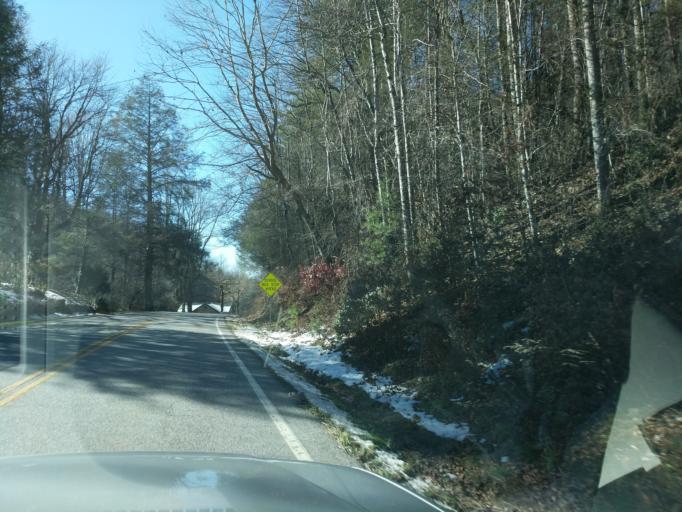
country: US
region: Georgia
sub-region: Rabun County
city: Clayton
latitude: 34.8623
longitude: -83.4977
